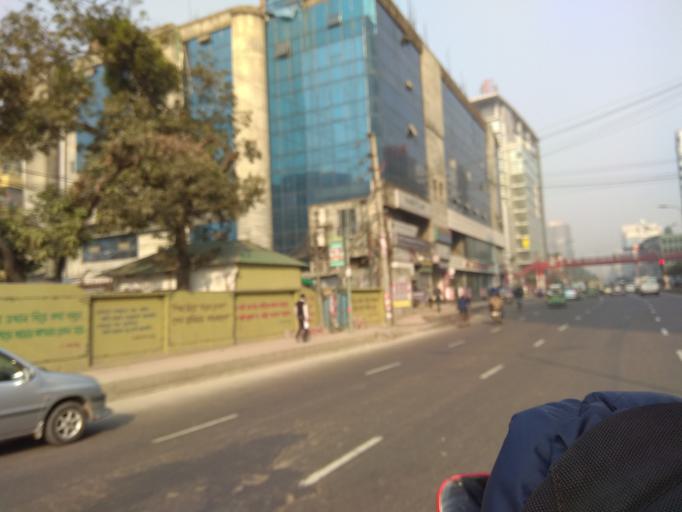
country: BD
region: Dhaka
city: Azimpur
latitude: 23.7450
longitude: 90.3950
